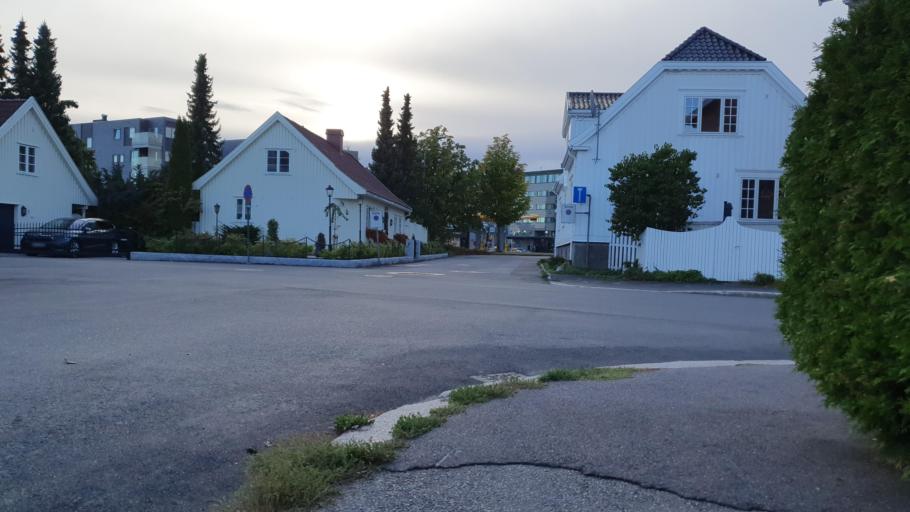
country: NO
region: Vestfold
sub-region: Tonsberg
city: Tonsberg
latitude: 59.2648
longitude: 10.4107
